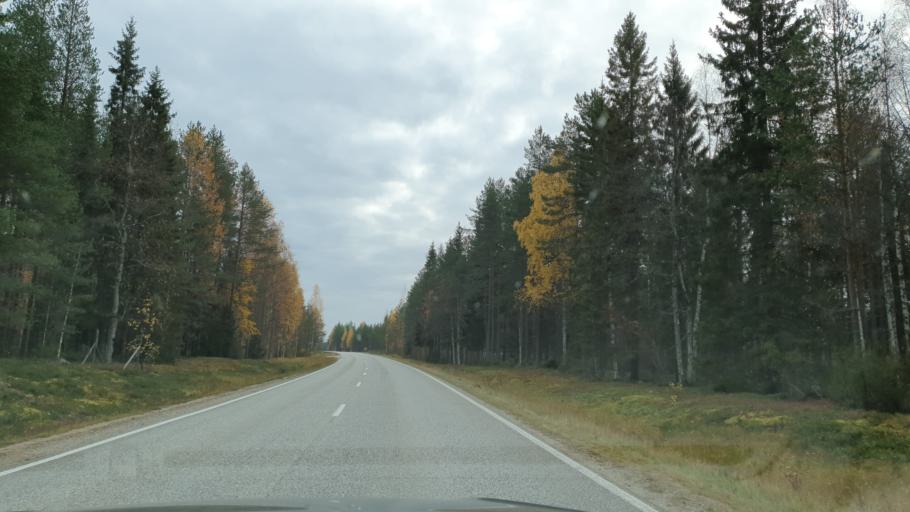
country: FI
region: Kainuu
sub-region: Kehys-Kainuu
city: Puolanka
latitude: 65.2418
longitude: 27.5829
